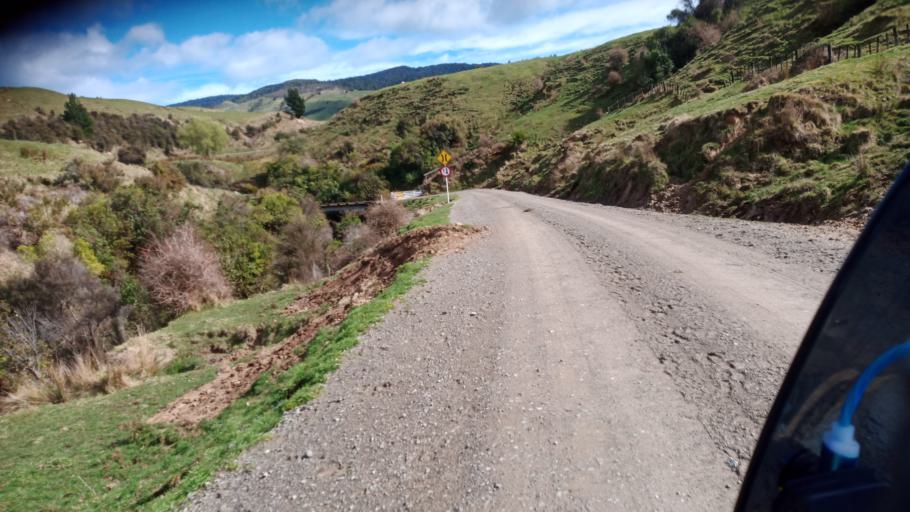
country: NZ
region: Hawke's Bay
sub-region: Wairoa District
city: Wairoa
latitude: -38.7352
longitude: 177.3018
